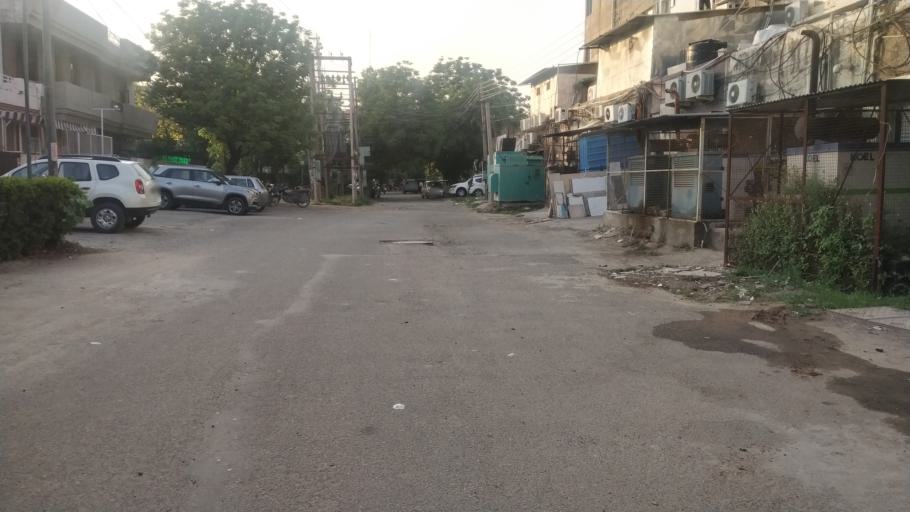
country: IN
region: Punjab
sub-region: Ajitgarh
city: Mohali
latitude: 30.7087
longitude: 76.7224
